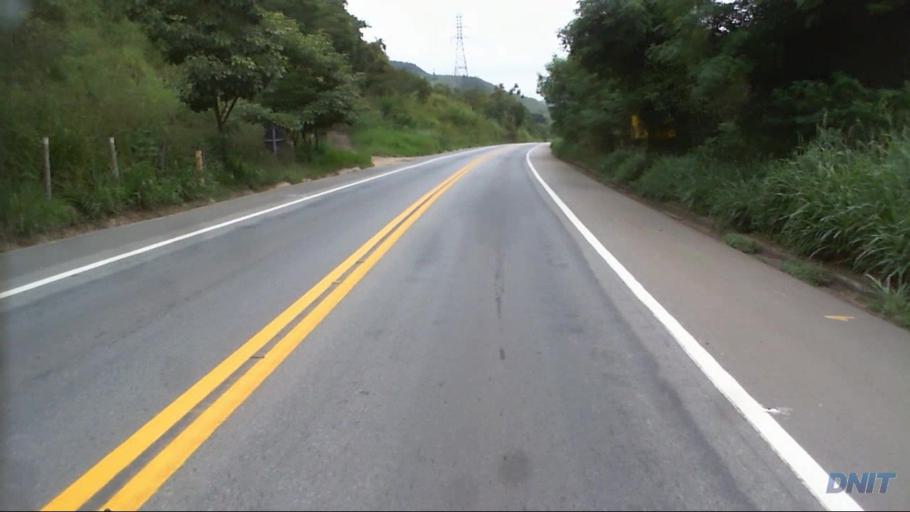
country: BR
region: Minas Gerais
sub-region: Timoteo
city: Timoteo
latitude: -19.5916
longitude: -42.7373
